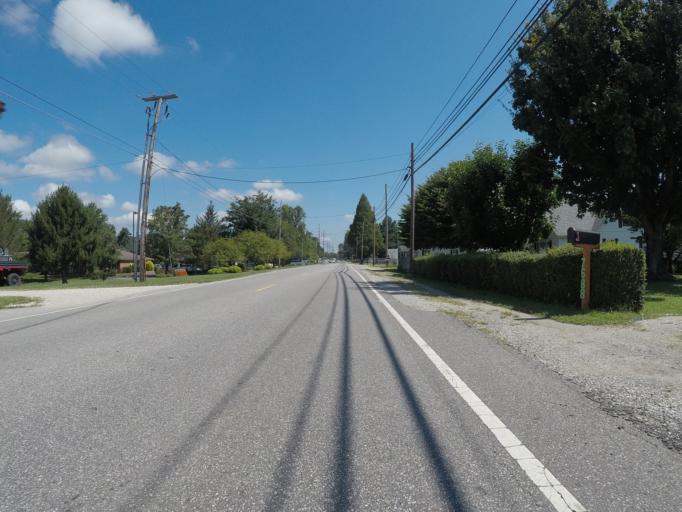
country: US
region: Ohio
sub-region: Lawrence County
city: Burlington
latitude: 38.4085
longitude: -82.5249
